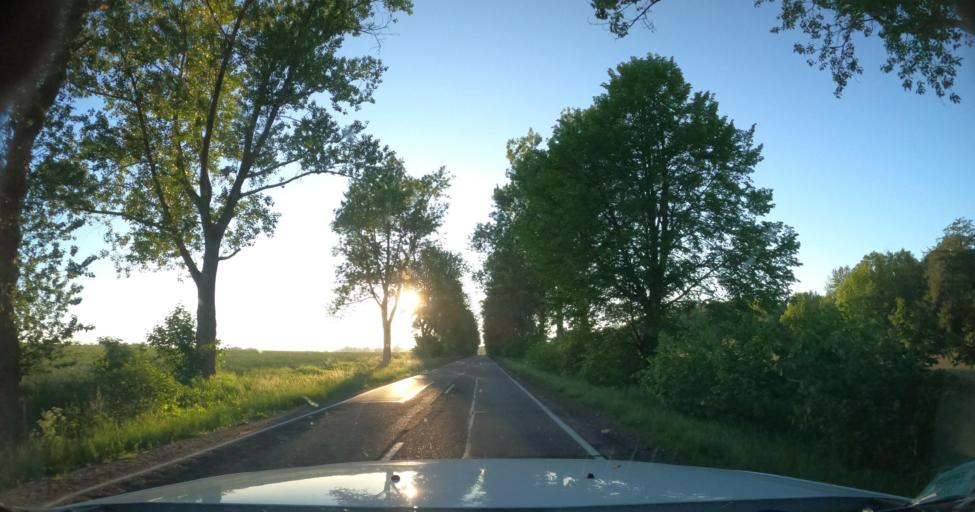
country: PL
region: Pomeranian Voivodeship
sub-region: Powiat slupski
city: Potegowo
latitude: 54.4145
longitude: 17.4125
